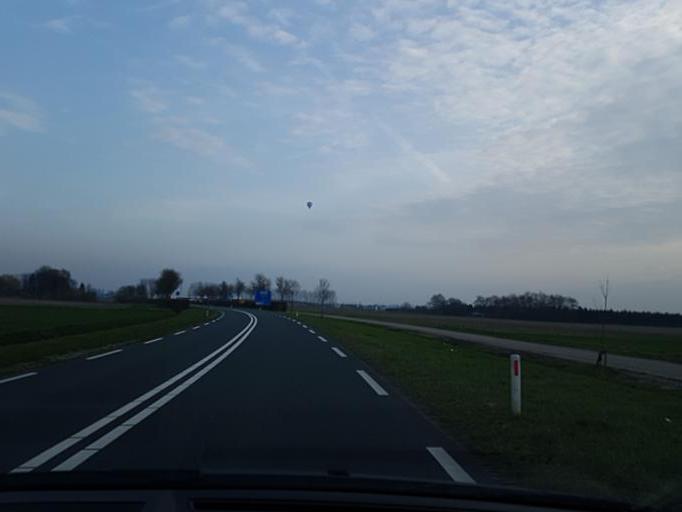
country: NL
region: Zeeland
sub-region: Gemeente Hulst
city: Hulst
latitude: 51.2793
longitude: 4.0362
